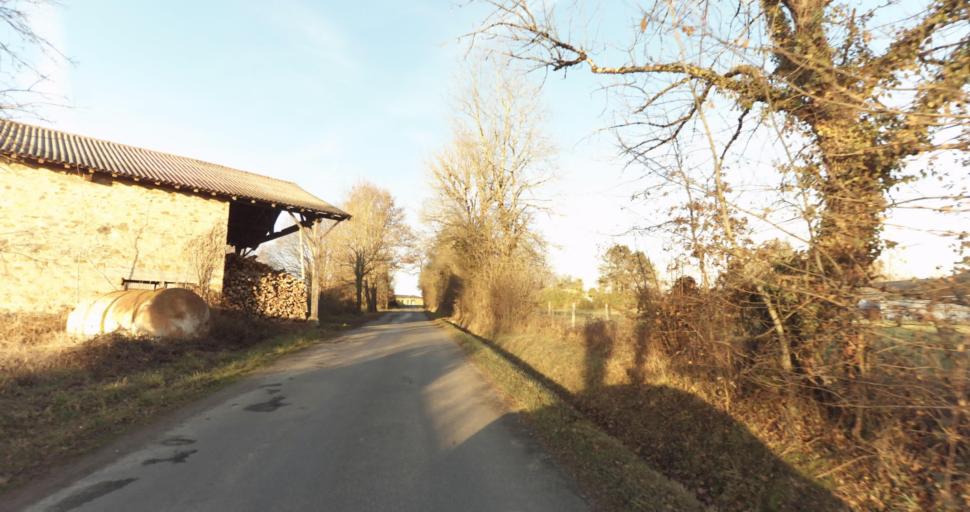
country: FR
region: Limousin
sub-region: Departement de la Haute-Vienne
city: Aixe-sur-Vienne
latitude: 45.8123
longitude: 1.1324
